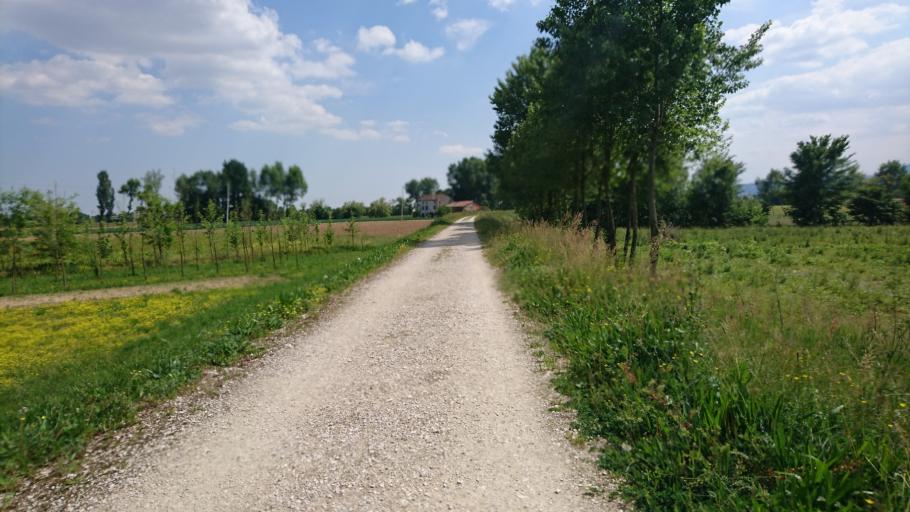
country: IT
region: Veneto
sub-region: Provincia di Padova
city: Veggiano
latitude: 45.4308
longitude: 11.7275
